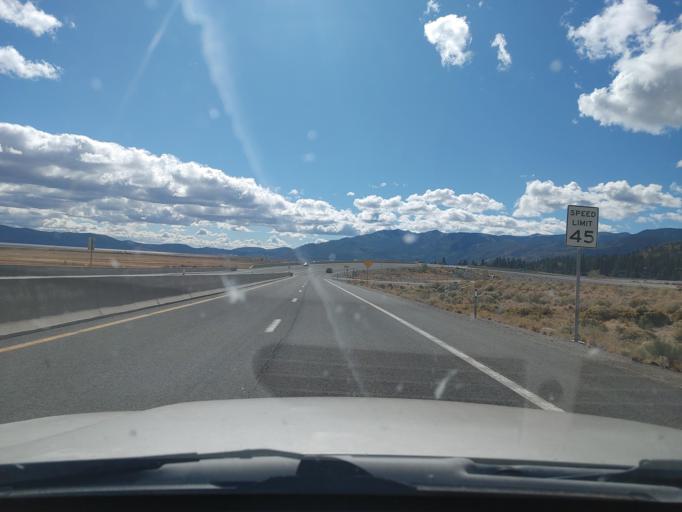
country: US
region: Nevada
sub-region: Carson City
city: Carson City
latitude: 39.3097
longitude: -119.8240
